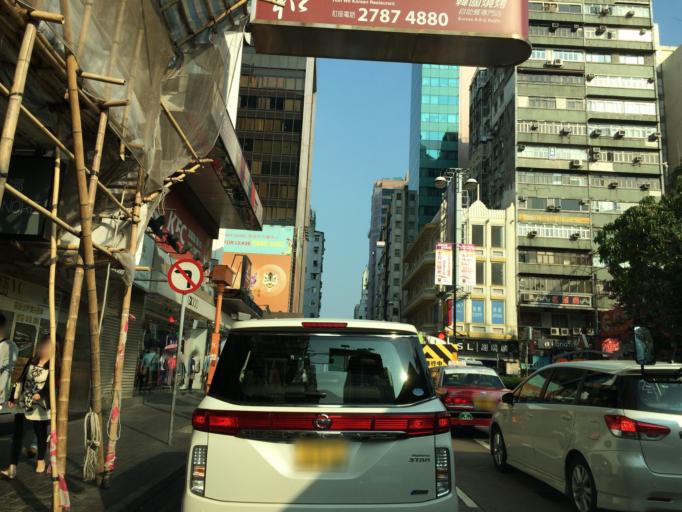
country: HK
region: Kowloon City
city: Kowloon
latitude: 22.3032
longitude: 114.1715
